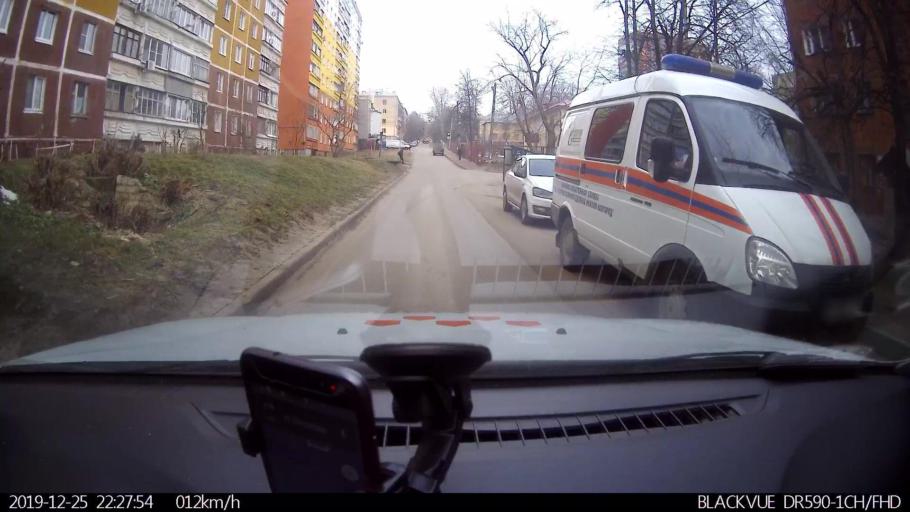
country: RU
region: Nizjnij Novgorod
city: Nizhniy Novgorod
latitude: 56.2655
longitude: 43.9772
